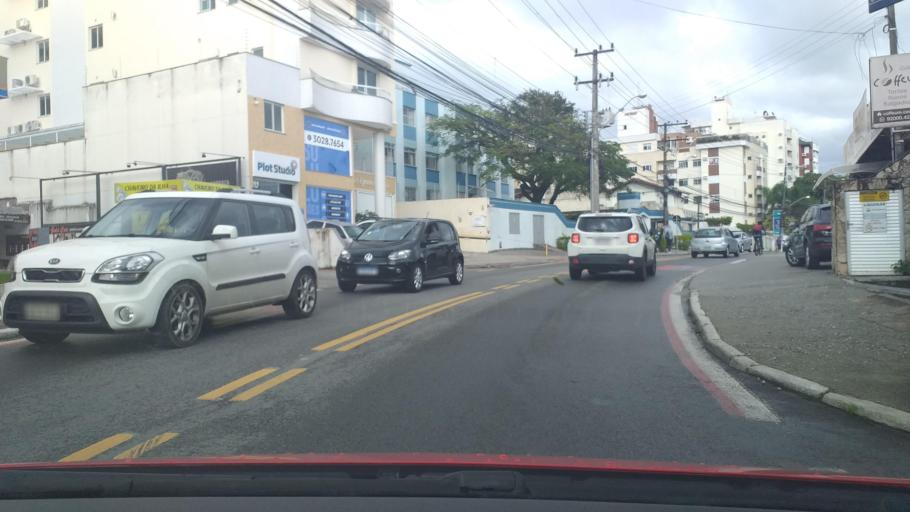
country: BR
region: Santa Catarina
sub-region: Florianopolis
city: Corrego Grande
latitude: -27.6007
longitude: -48.5135
